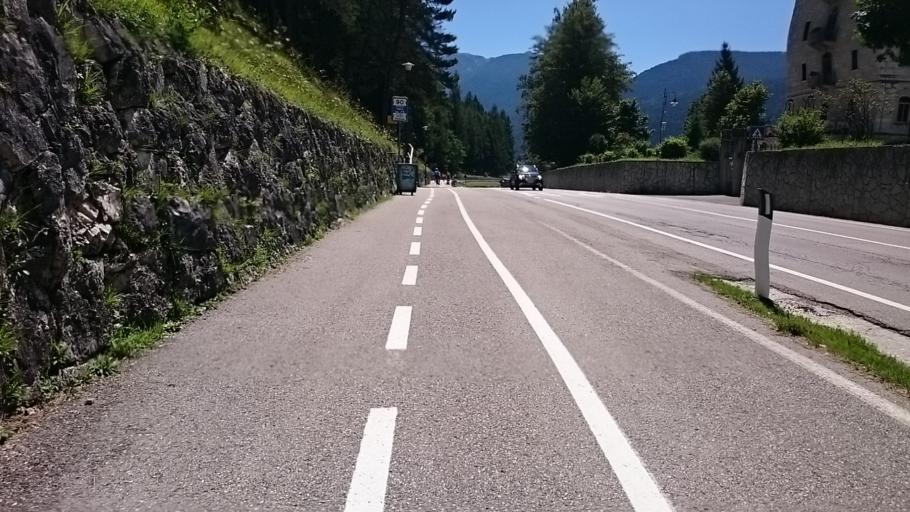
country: IT
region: Veneto
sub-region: Provincia di Belluno
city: San Vito
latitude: 46.4471
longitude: 12.2110
